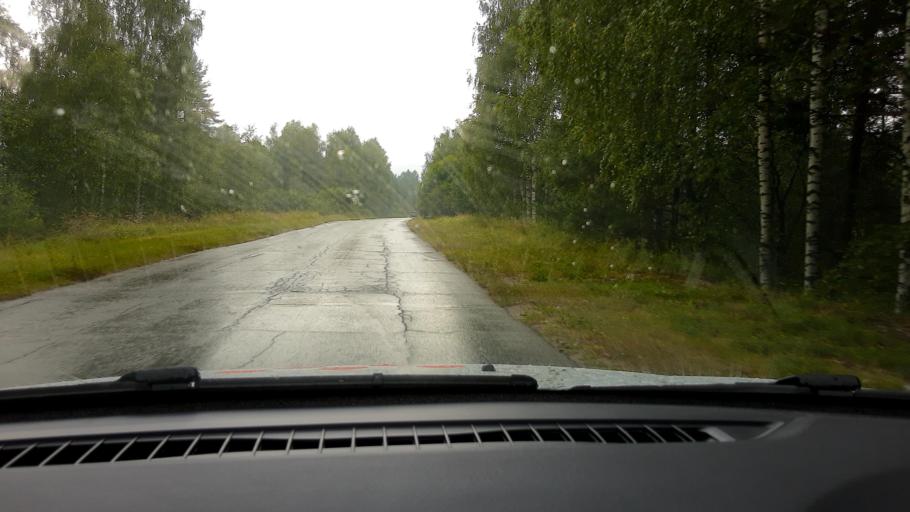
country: RU
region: Nizjnij Novgorod
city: Dal'neye Konstantinovo
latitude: 55.9506
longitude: 43.9638
